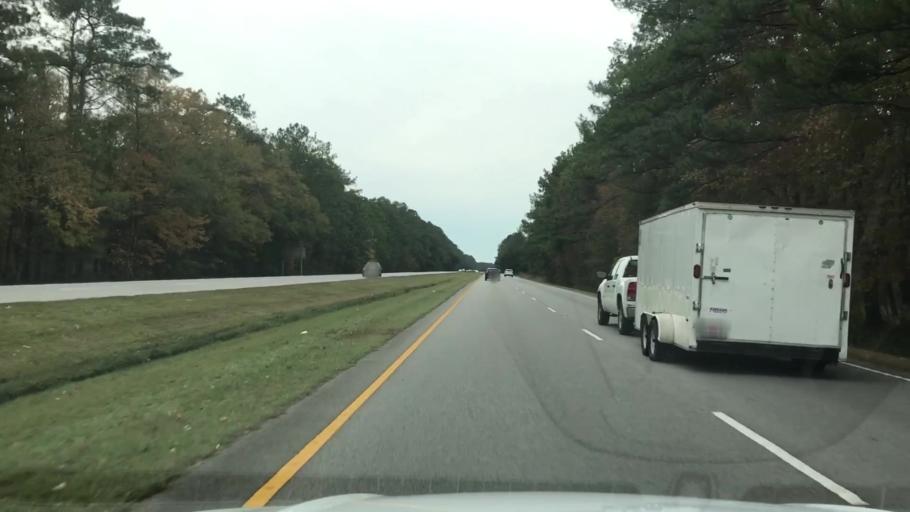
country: US
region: South Carolina
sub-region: Georgetown County
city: Georgetown
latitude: 33.4017
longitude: -79.2004
